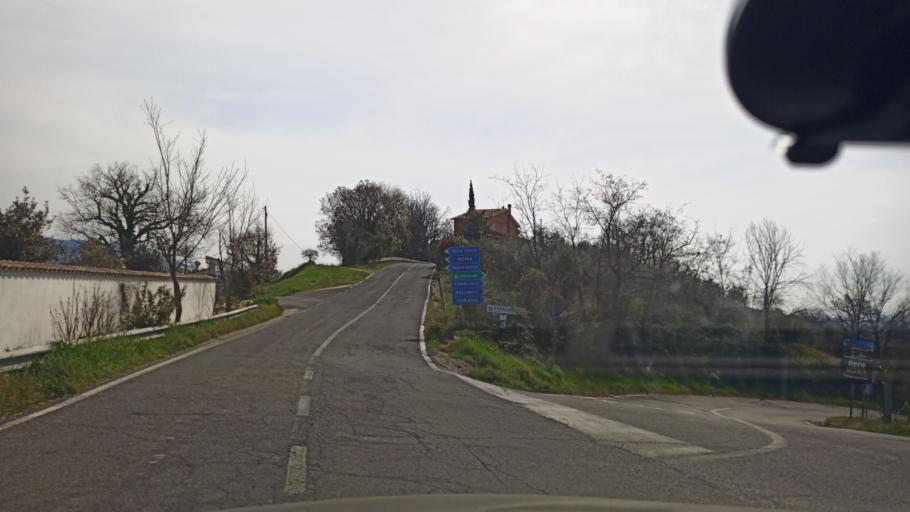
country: IT
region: Latium
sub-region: Provincia di Rieti
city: Torri in Sabina
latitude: 42.3482
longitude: 12.6496
